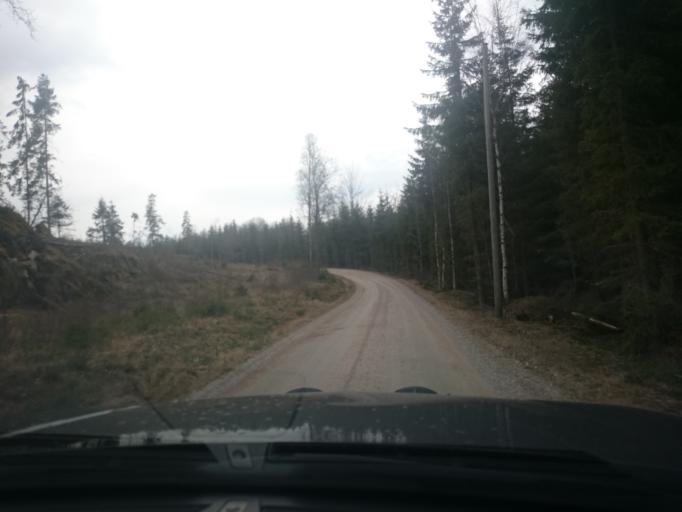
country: SE
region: Joenkoeping
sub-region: Vetlanda Kommun
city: Vetlanda
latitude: 57.2959
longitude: 15.1378
